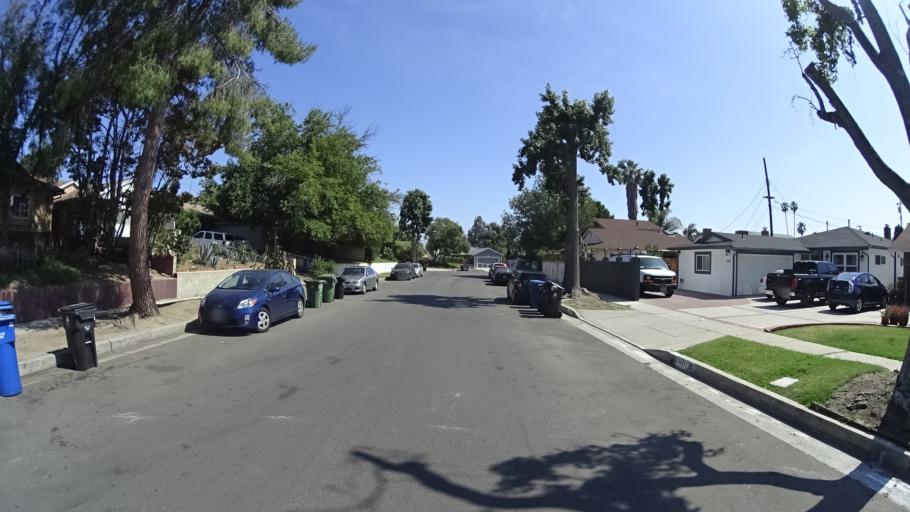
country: US
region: California
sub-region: Los Angeles County
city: Van Nuys
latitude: 34.1982
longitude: -118.4193
